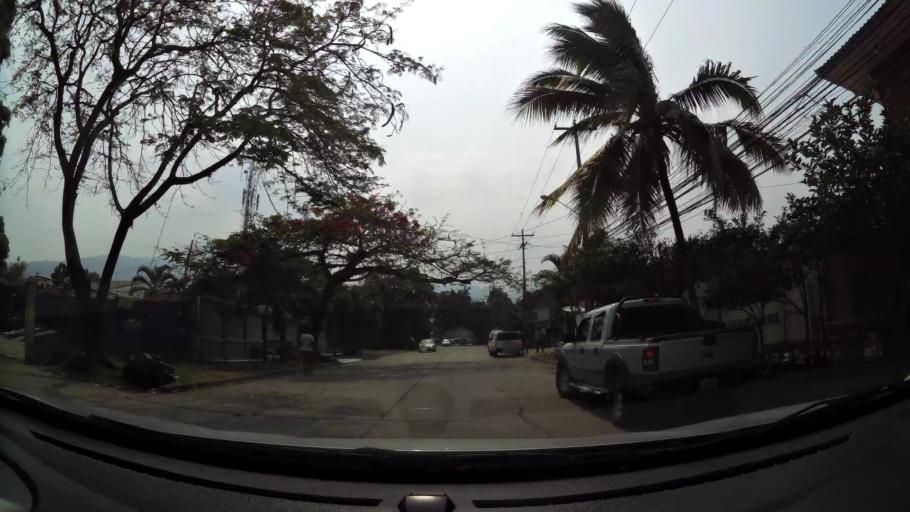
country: HN
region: Cortes
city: San Pedro Sula
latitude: 15.4891
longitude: -88.0312
